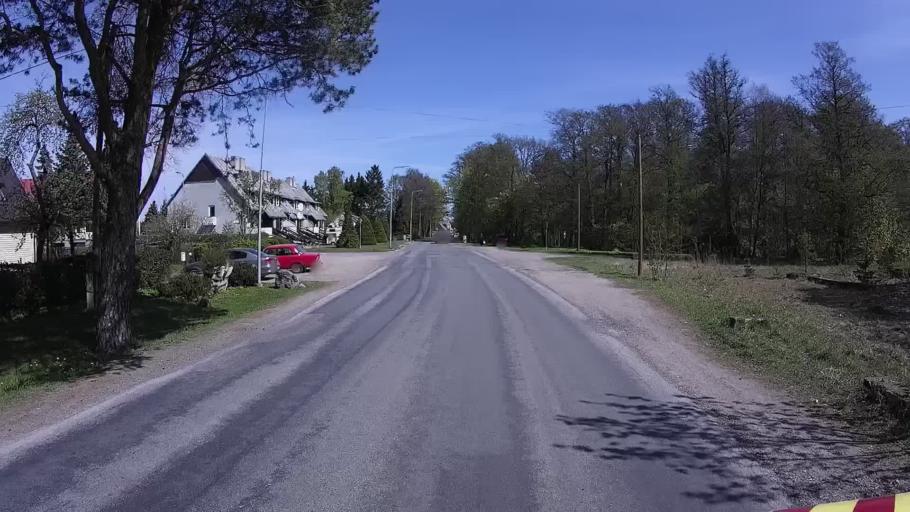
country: EE
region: Laeaene
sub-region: Haapsalu linn
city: Haapsalu
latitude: 58.9356
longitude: 23.5622
